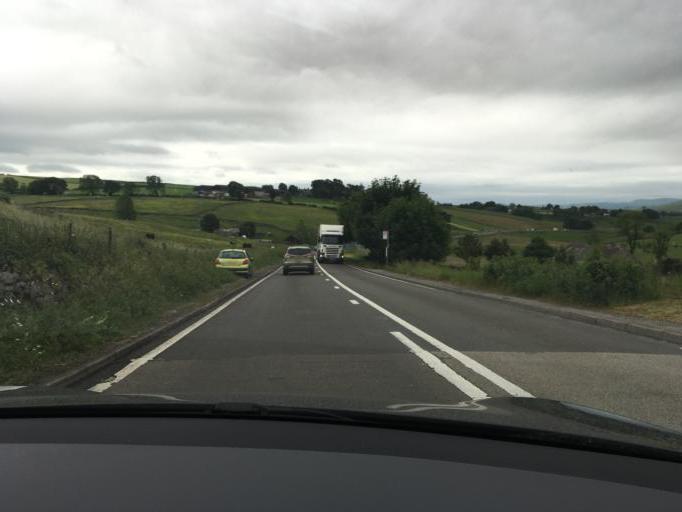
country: GB
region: England
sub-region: Derbyshire
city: Chapel en le Frith
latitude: 53.3229
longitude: -1.8653
